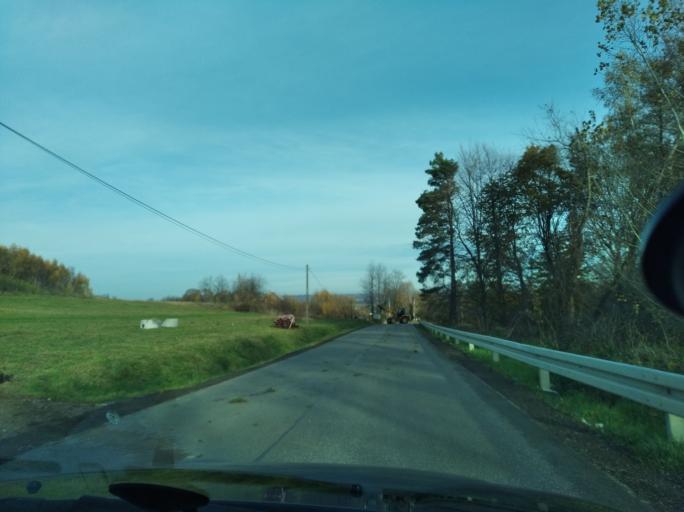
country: PL
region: Subcarpathian Voivodeship
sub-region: Powiat rzeszowski
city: Siedliska
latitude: 49.9408
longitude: 21.9783
